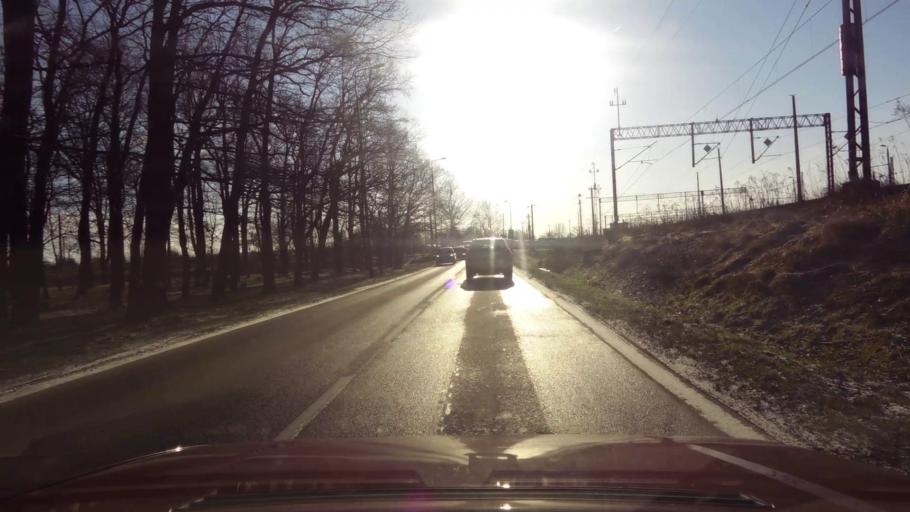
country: PL
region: West Pomeranian Voivodeship
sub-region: Powiat bialogardzki
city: Bialogard
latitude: 54.0172
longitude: 15.9778
